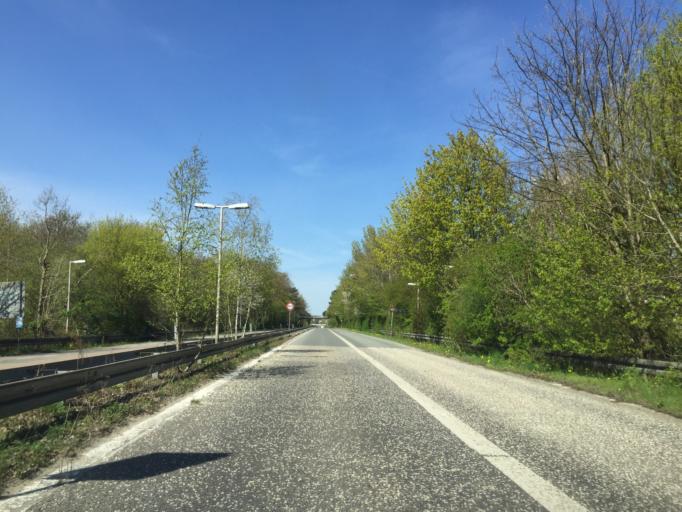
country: DK
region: Capital Region
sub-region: Gladsaxe Municipality
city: Buddinge
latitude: 55.7208
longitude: 12.4989
